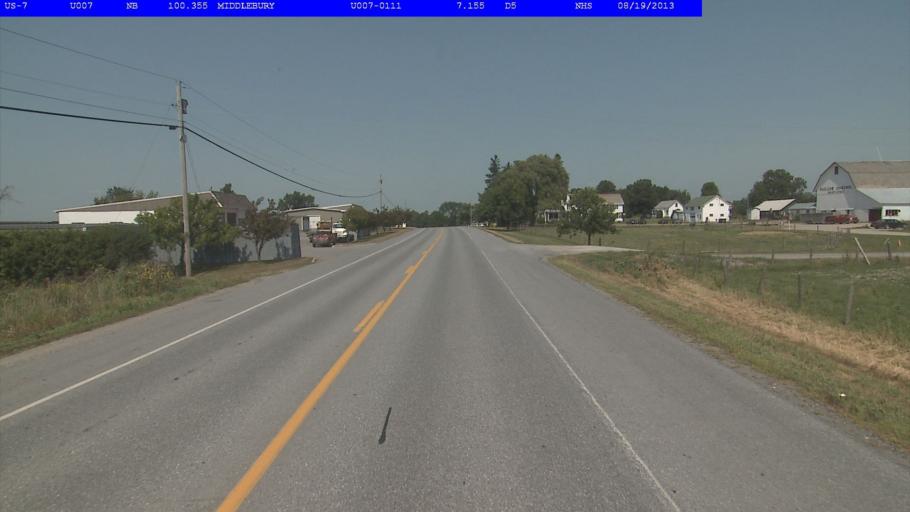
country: US
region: Vermont
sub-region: Addison County
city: Middlebury (village)
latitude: 44.0424
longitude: -73.1622
